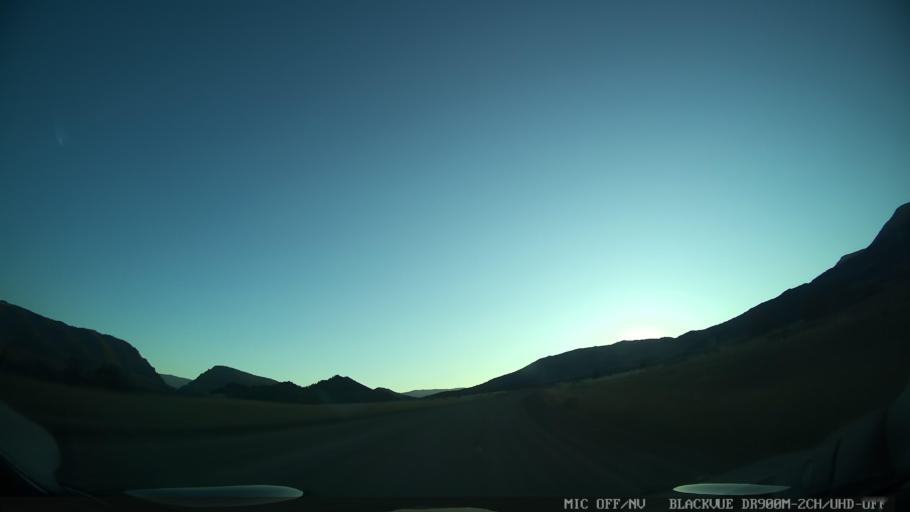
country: US
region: Colorado
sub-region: Eagle County
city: Edwards
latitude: 39.8993
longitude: -106.6058
